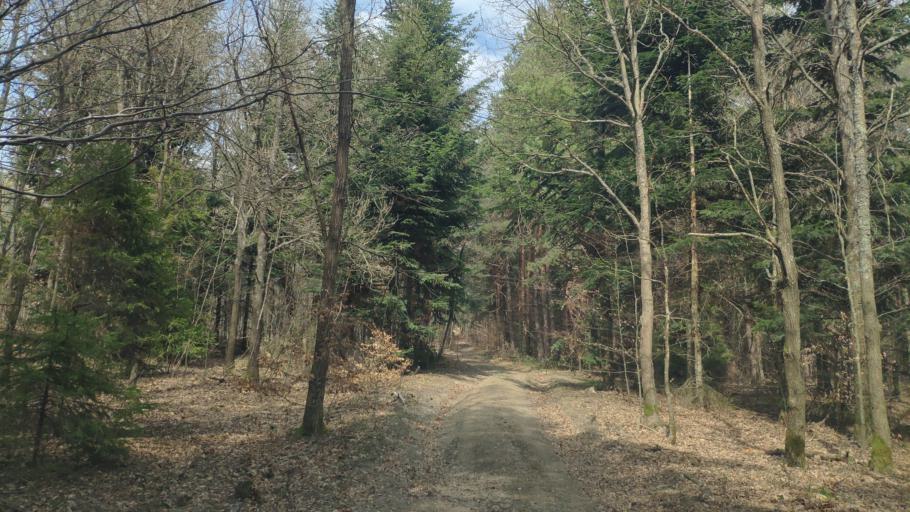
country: SK
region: Kosicky
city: Gelnica
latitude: 48.7540
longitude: 21.0207
